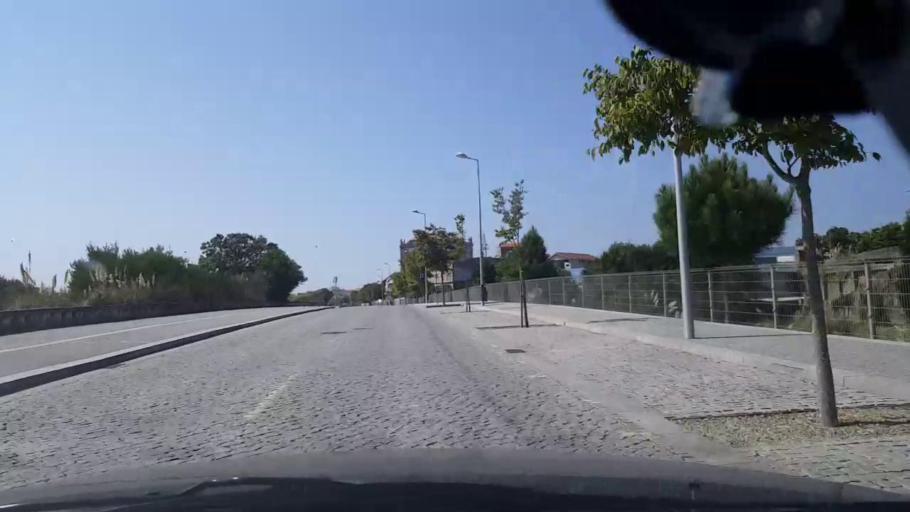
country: PT
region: Porto
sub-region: Vila do Conde
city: Vila do Conde
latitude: 41.3523
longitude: -8.7333
